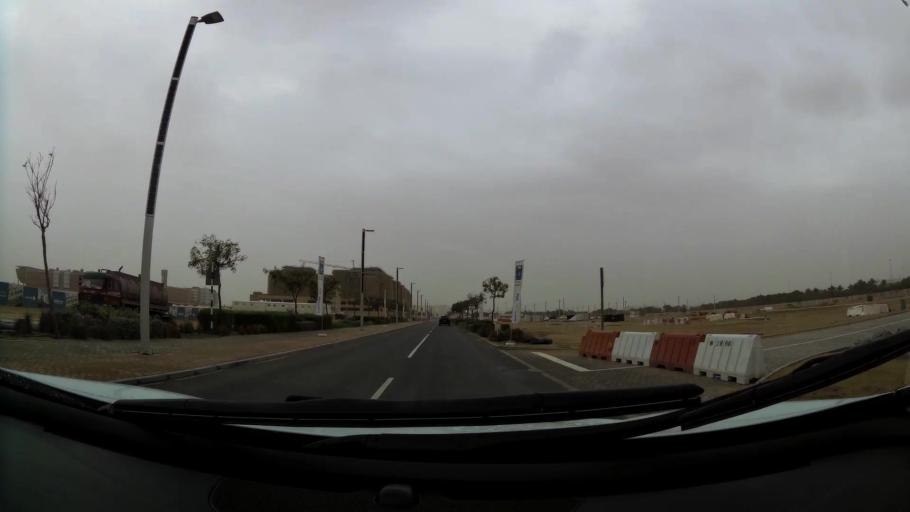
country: AE
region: Abu Dhabi
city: Abu Dhabi
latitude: 24.4338
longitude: 54.6240
